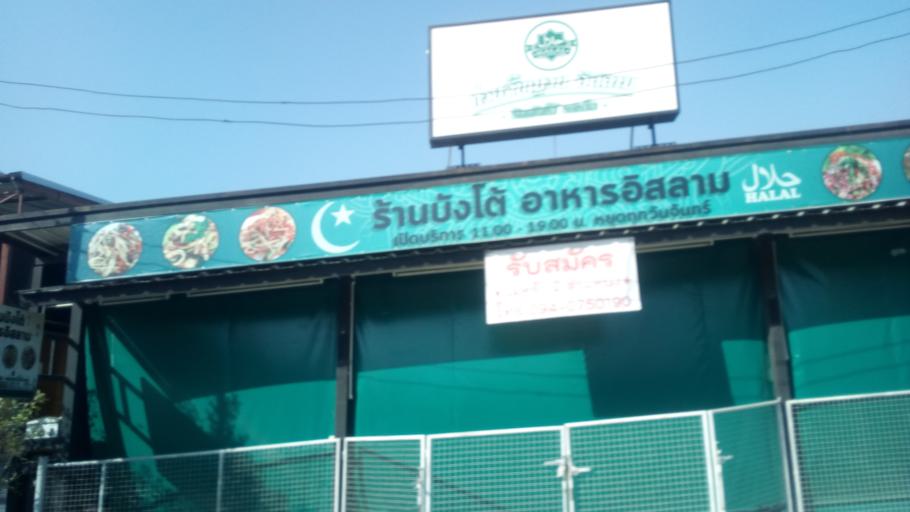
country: TH
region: Nonthaburi
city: Bang Bua Thong
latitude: 13.9367
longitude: 100.3678
